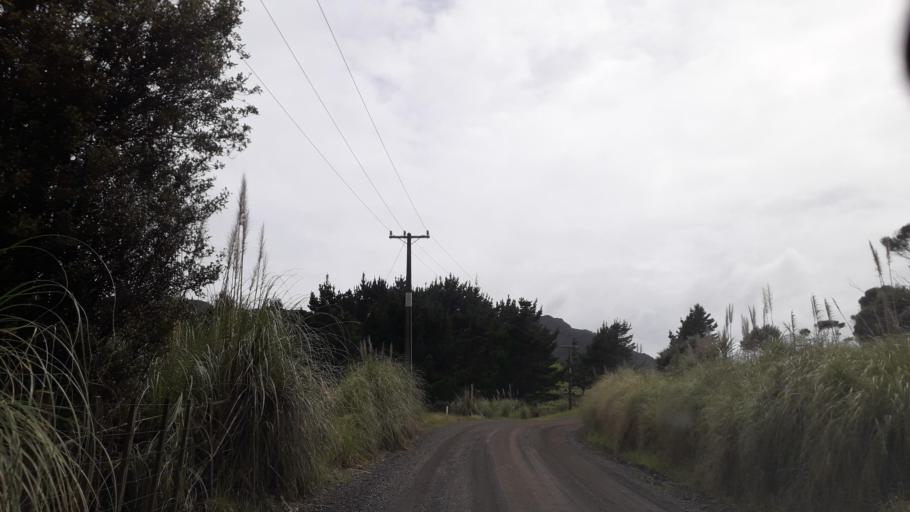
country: NZ
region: Northland
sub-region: Far North District
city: Ahipara
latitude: -35.4349
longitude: 173.3319
